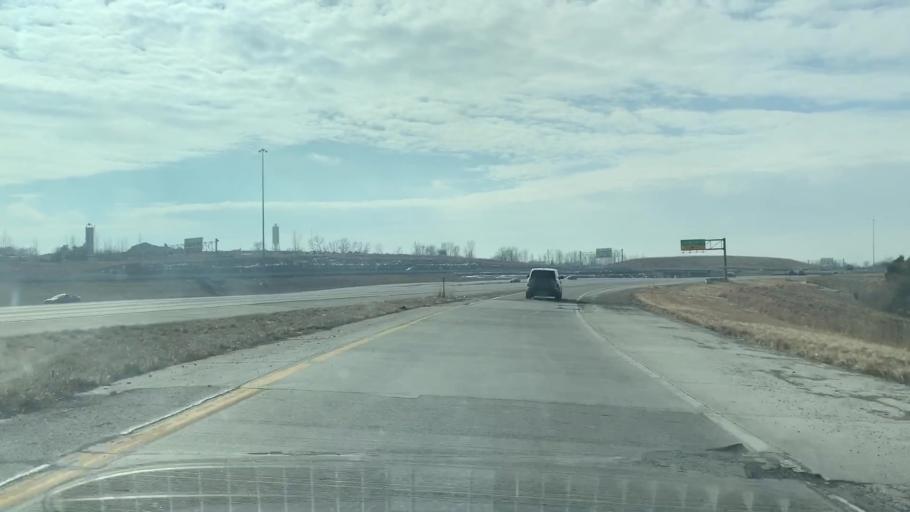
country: US
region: Kansas
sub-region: Johnson County
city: Lenexa
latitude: 38.9442
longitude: -94.7762
